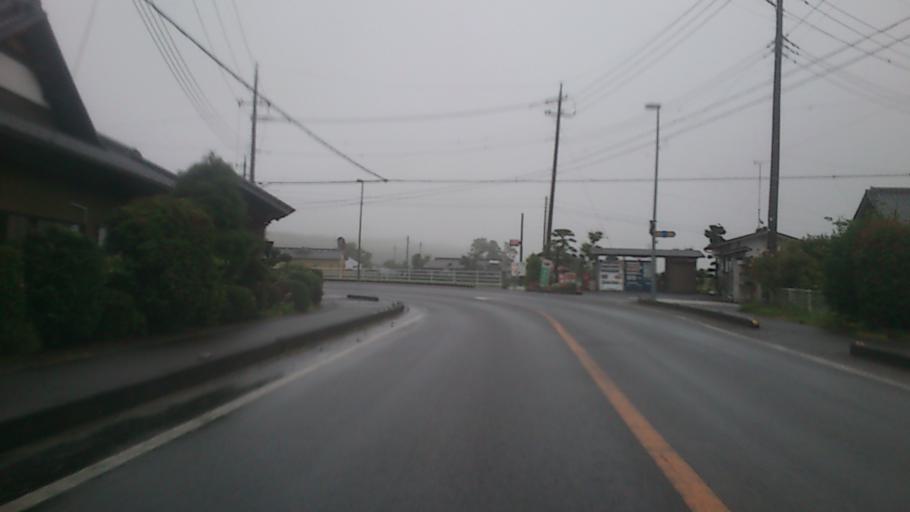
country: JP
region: Tochigi
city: Otawara
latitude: 36.8498
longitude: 140.0461
